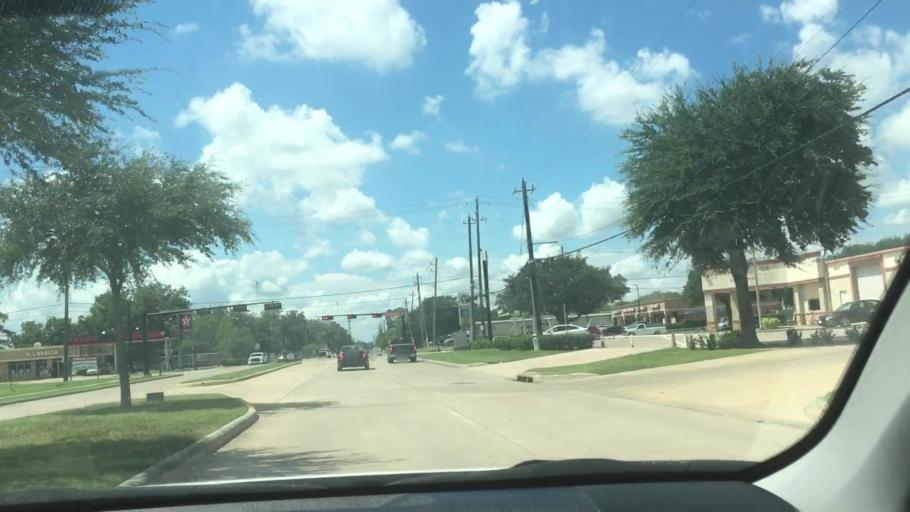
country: US
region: Texas
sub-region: Fort Bend County
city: Fifth Street
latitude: 29.6054
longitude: -95.5479
